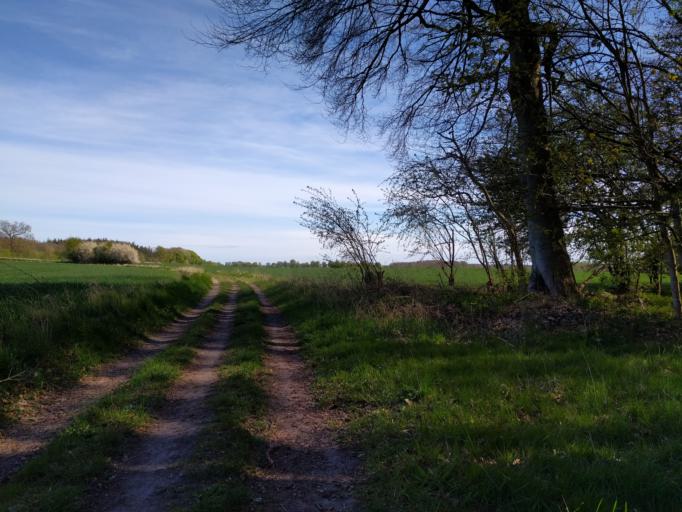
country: DK
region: South Denmark
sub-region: Kerteminde Kommune
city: Munkebo
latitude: 55.4301
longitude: 10.5551
